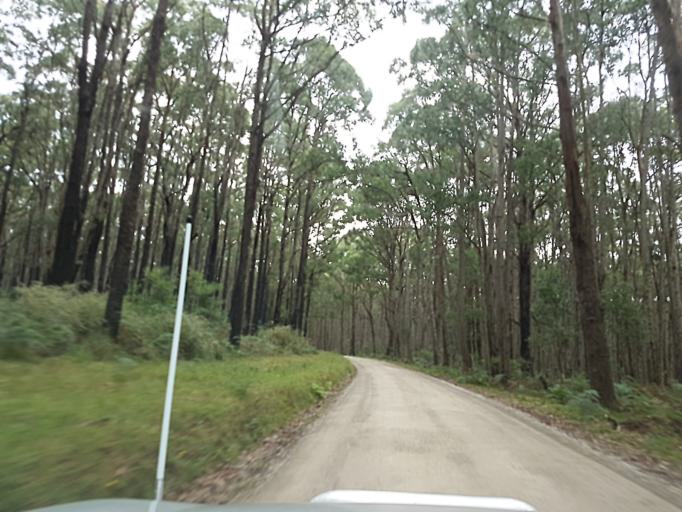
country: AU
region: Victoria
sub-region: Yarra Ranges
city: Mount Dandenong
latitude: -37.8314
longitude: 145.3977
